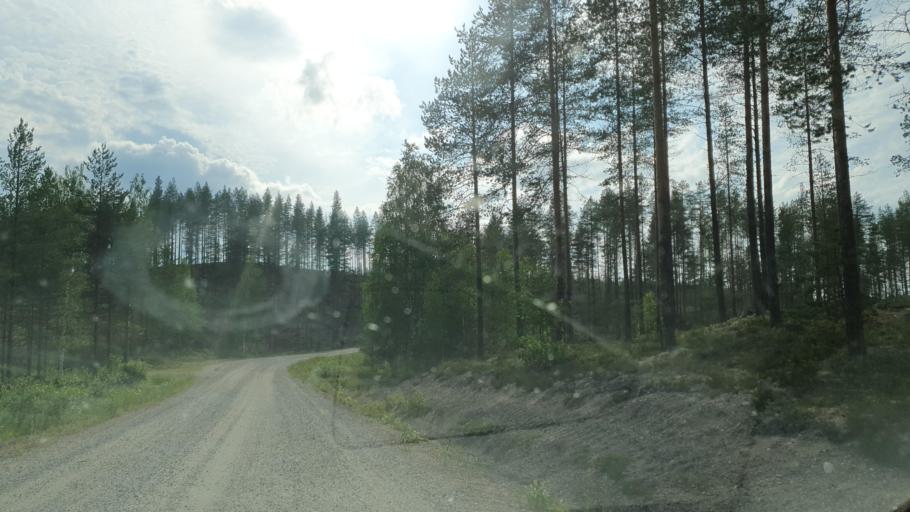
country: FI
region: Kainuu
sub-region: Kehys-Kainuu
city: Kuhmo
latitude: 64.0207
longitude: 29.8988
